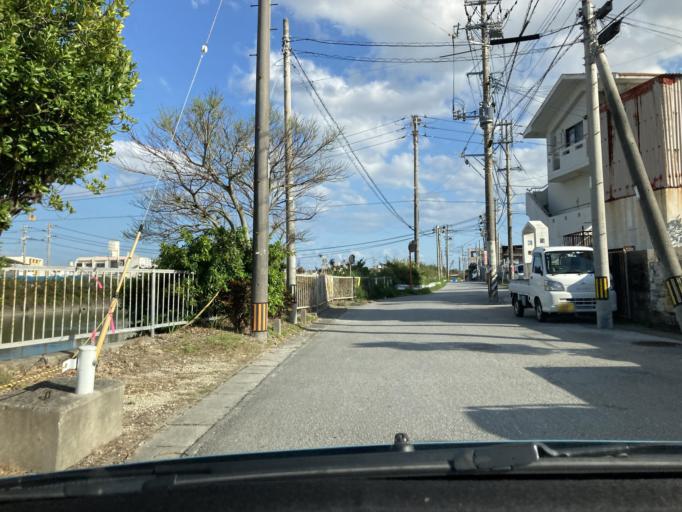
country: JP
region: Okinawa
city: Tomigusuku
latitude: 26.1946
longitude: 127.7002
